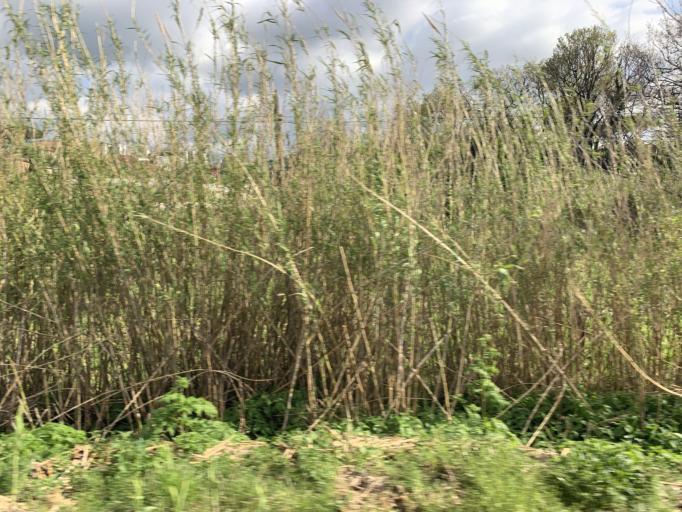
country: IT
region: Latium
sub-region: Citta metropolitana di Roma Capitale
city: Marino
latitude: 41.7765
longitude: 12.6384
